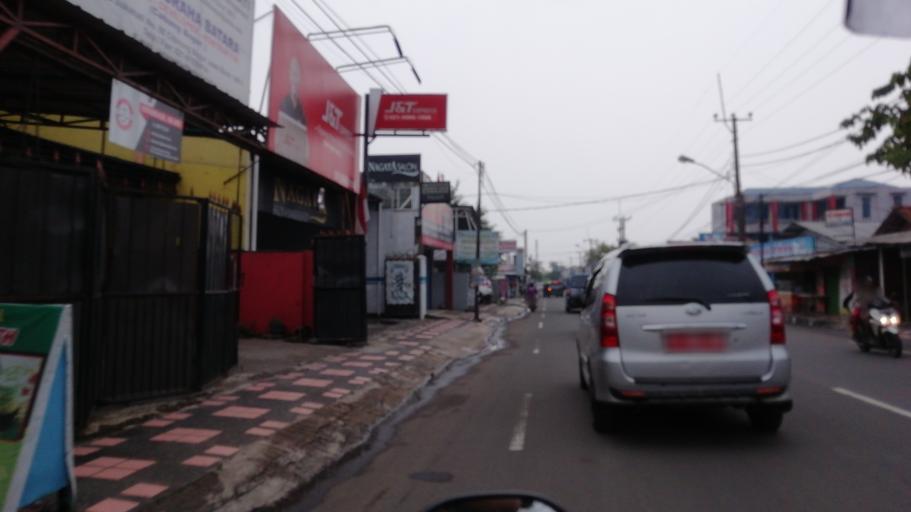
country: ID
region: West Java
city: Cibinong
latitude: -6.4988
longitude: 106.8107
